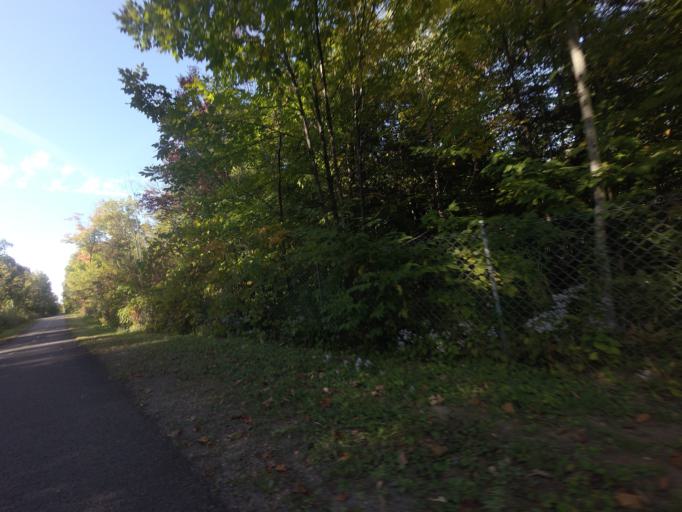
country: CA
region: Quebec
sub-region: Laurentides
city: Saint-Jerome
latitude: 45.7294
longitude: -73.9420
